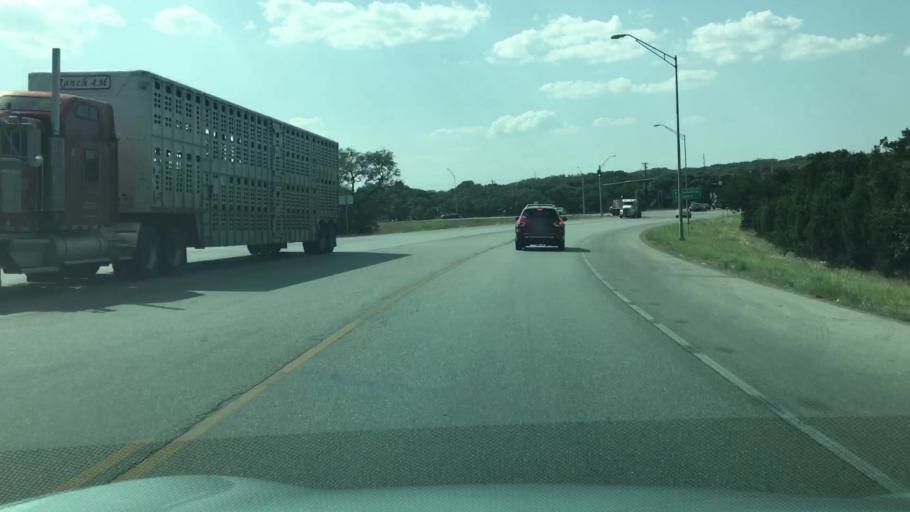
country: US
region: Texas
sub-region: Hays County
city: Wimberley
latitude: 29.9414
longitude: -98.0906
